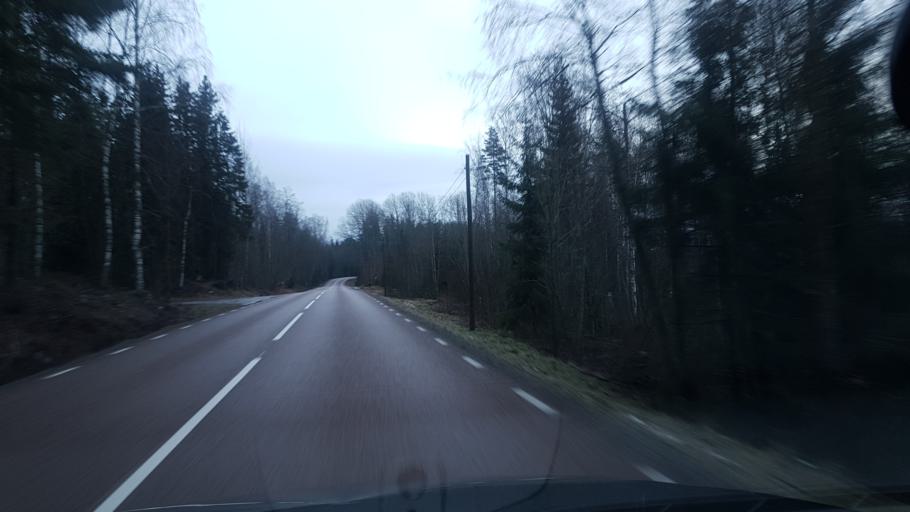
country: SE
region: Dalarna
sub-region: Saters Kommun
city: Saeter
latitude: 60.4140
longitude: 15.6895
